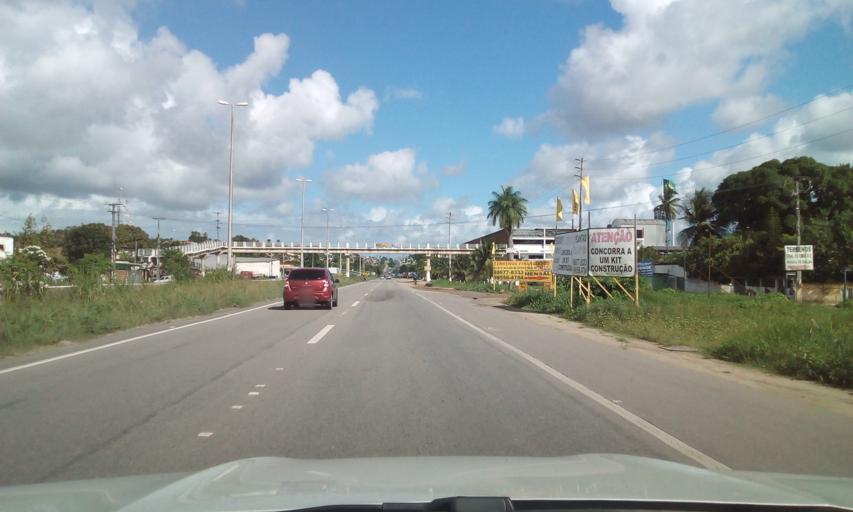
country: BR
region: Pernambuco
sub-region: Igarassu
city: Igarassu
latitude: -7.8295
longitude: -34.9145
